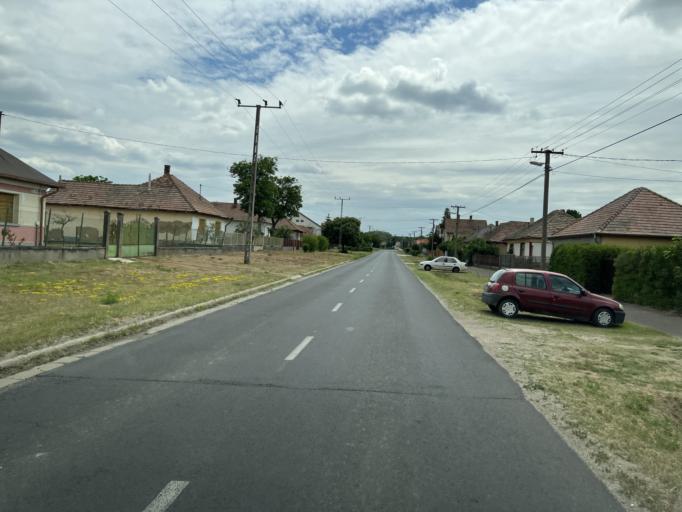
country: HU
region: Pest
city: Koka
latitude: 47.4836
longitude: 19.5942
